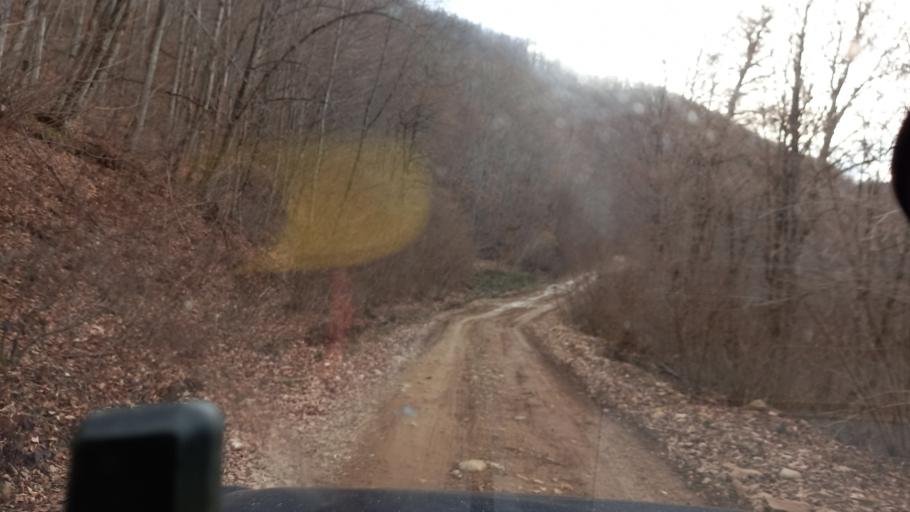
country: RU
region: Adygeya
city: Kamennomostskiy
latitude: 44.1762
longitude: 40.2998
